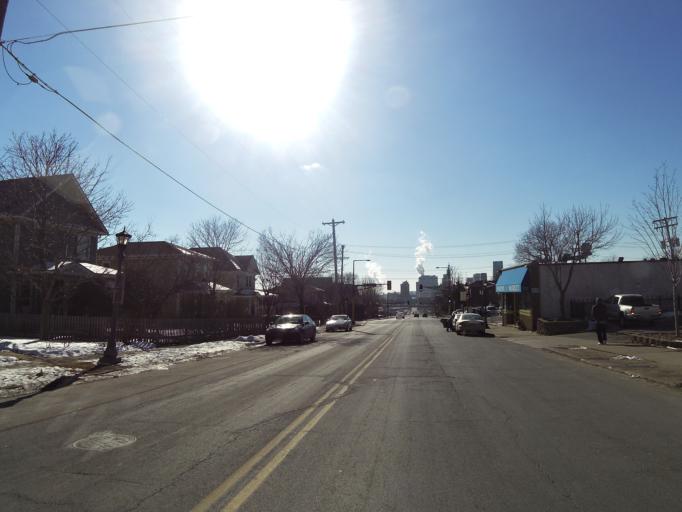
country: US
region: Minnesota
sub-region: Ramsey County
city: Saint Paul
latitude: 44.9554
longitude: -93.0695
